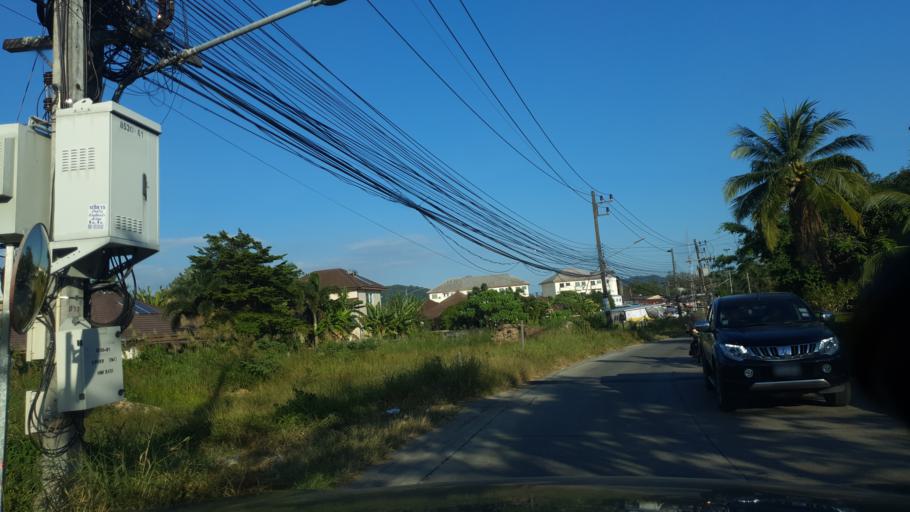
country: TH
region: Phuket
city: Kathu
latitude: 7.9033
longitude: 98.3334
